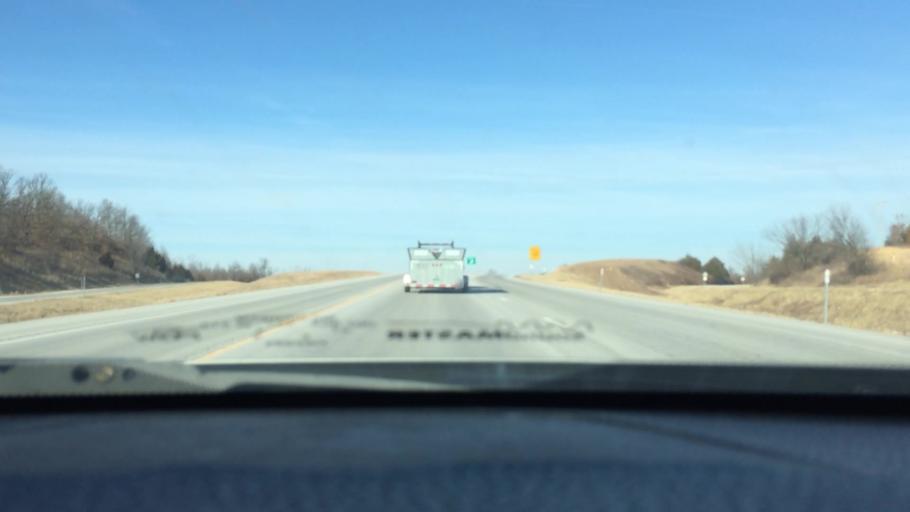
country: US
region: Missouri
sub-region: Newton County
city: Neosho
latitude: 36.9013
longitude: -94.3167
